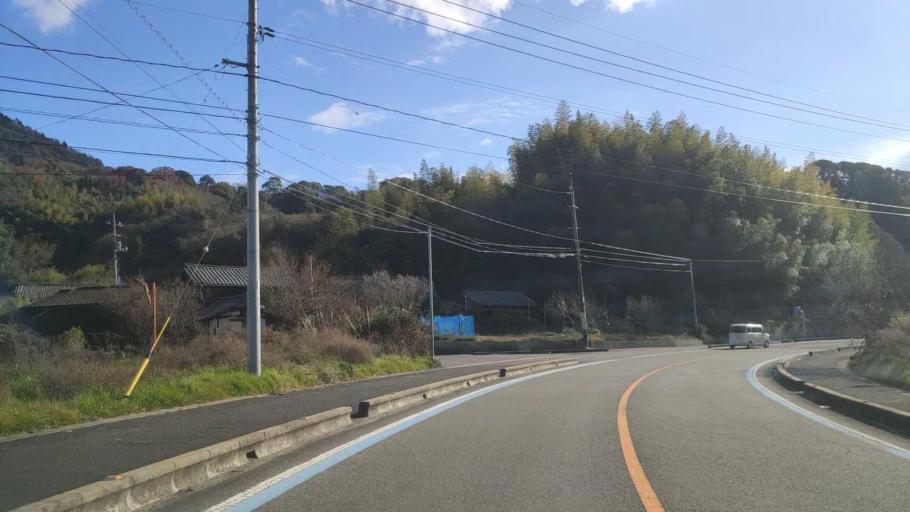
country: JP
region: Hiroshima
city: Innoshima
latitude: 34.2207
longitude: 133.0685
